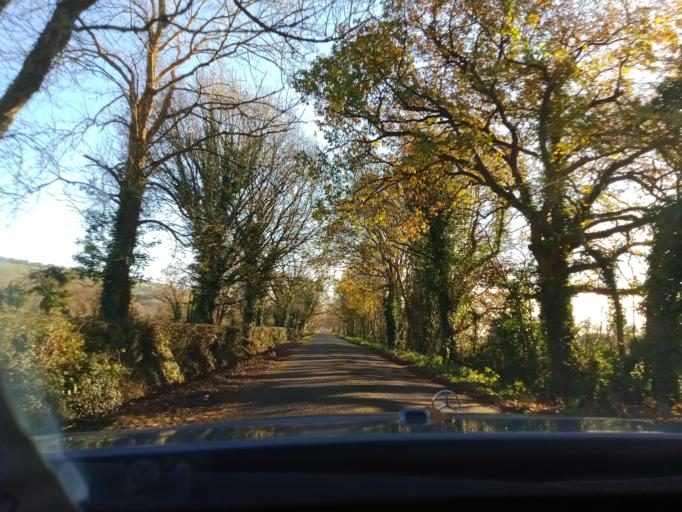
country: IE
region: Leinster
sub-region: Kilkenny
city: Piltown
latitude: 52.3535
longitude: -7.2927
